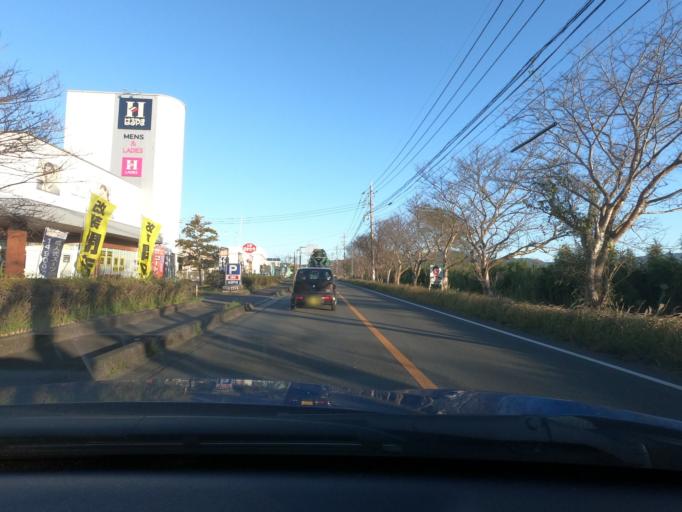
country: JP
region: Kagoshima
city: Satsumasendai
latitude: 31.8097
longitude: 130.3172
